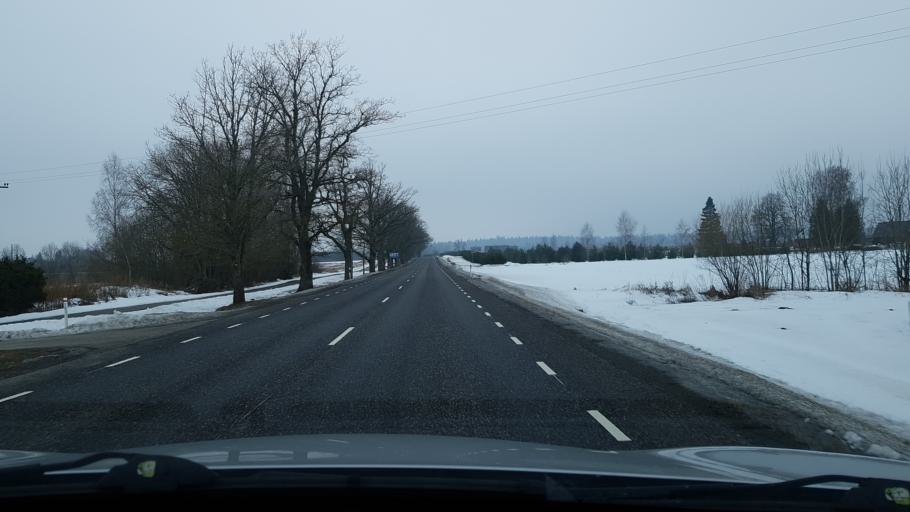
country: EE
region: Vorumaa
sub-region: Antsla vald
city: Vana-Antsla
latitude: 57.9126
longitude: 26.3009
